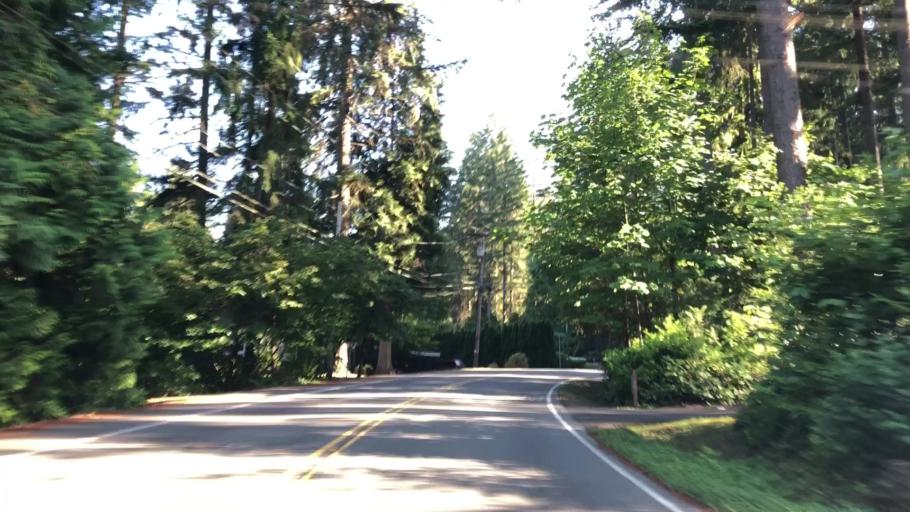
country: US
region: Washington
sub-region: King County
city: Cottage Lake
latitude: 47.7598
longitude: -122.1172
